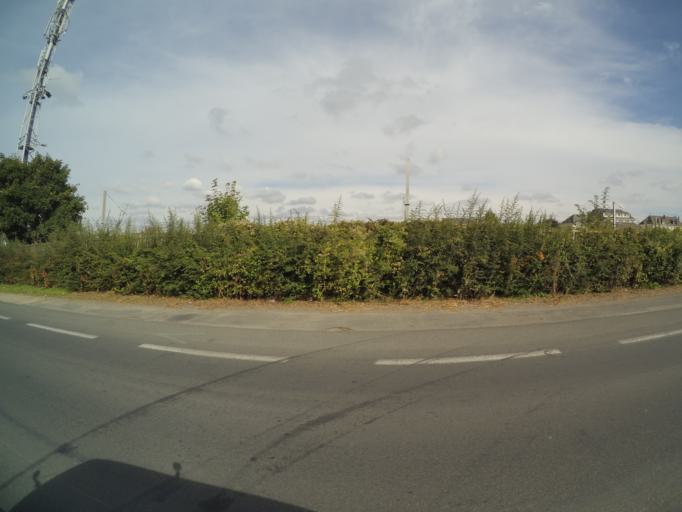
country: FR
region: Pays de la Loire
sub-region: Departement de Maine-et-Loire
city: Saumur
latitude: 47.2689
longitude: -0.0730
